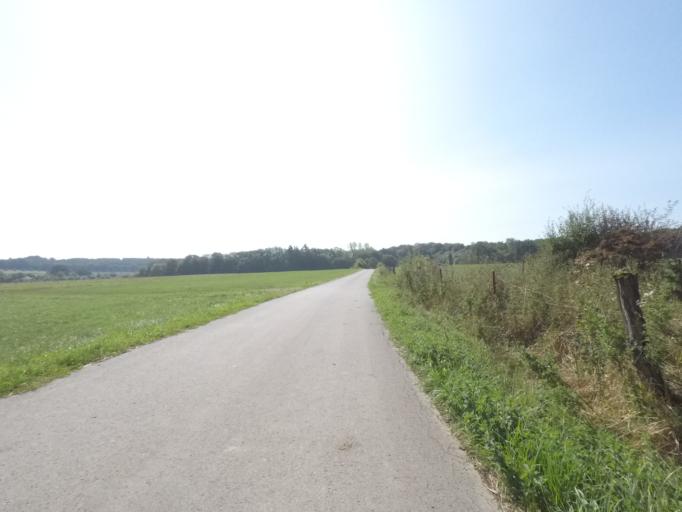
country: LU
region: Luxembourg
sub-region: Canton de Luxembourg
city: Olm
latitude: 49.6572
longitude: 6.0177
